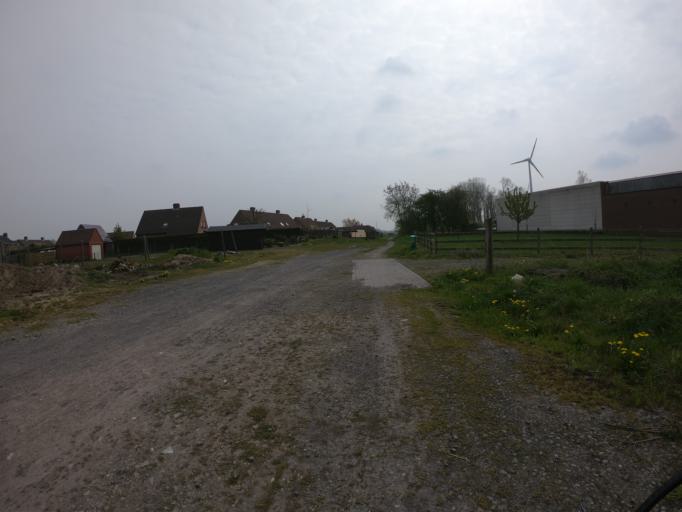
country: BE
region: Flanders
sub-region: Provincie West-Vlaanderen
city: Avelgem
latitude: 50.7690
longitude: 3.4460
